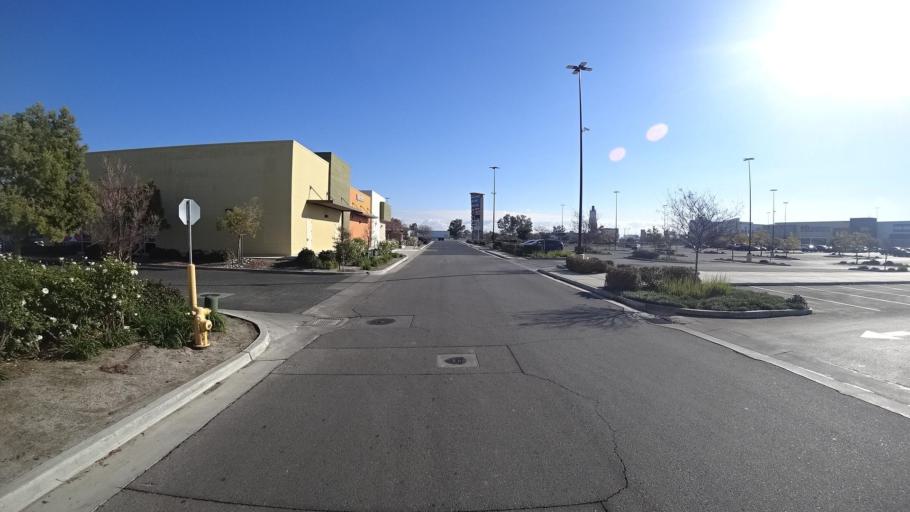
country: US
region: California
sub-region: Kern County
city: Delano
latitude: 35.7458
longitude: -119.2457
